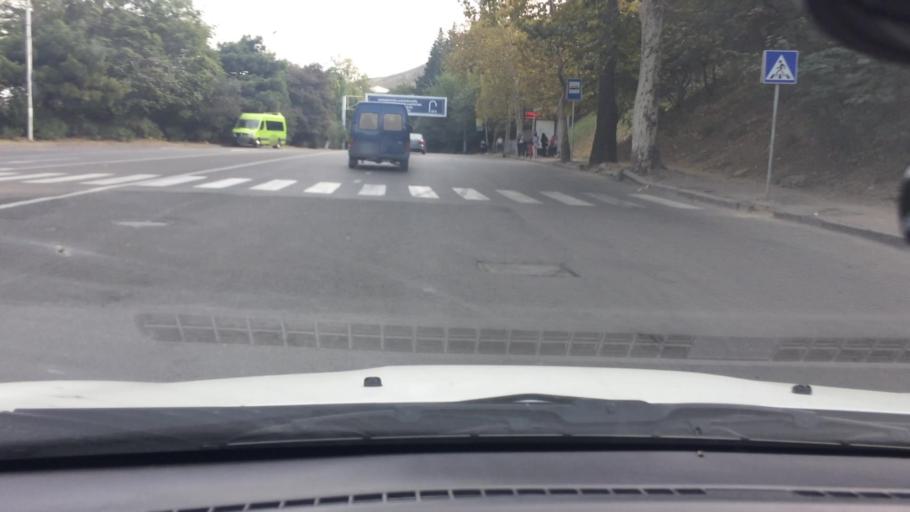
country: GE
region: T'bilisi
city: Tbilisi
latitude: 41.6724
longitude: 44.8344
